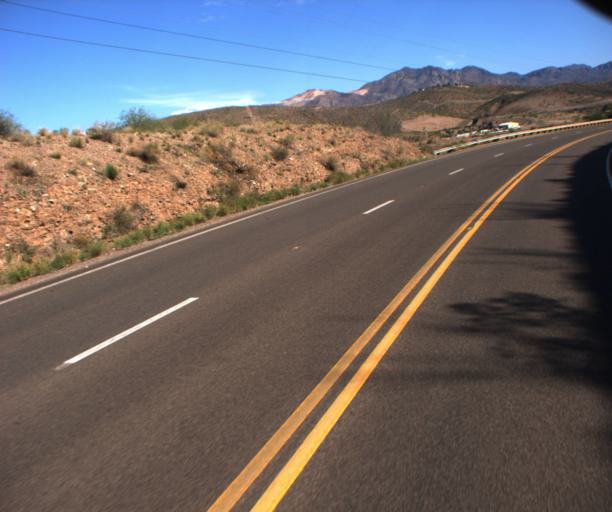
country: US
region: Arizona
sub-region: Greenlee County
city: Clifton
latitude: 33.0307
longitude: -109.2993
